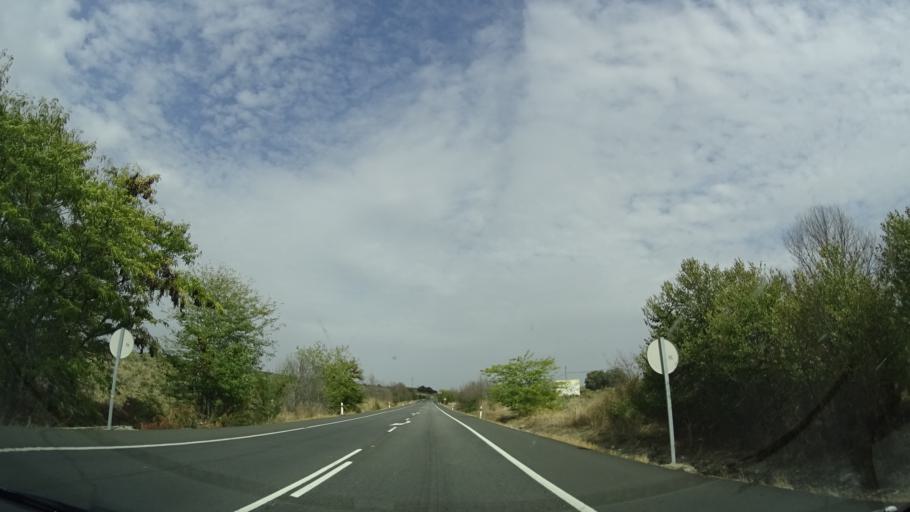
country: ES
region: Extremadura
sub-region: Provincia de Caceres
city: Trujillo
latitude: 39.4355
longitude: -5.8906
